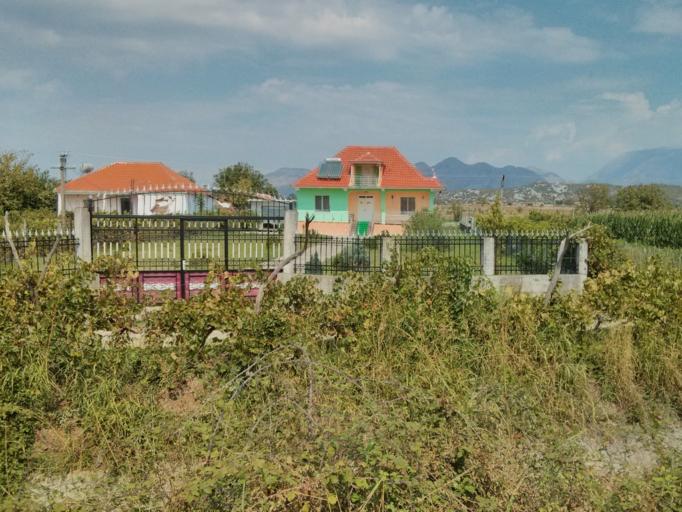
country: AL
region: Shkoder
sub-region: Rrethi i Malesia e Madhe
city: Gruemire
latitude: 42.1442
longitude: 19.5253
